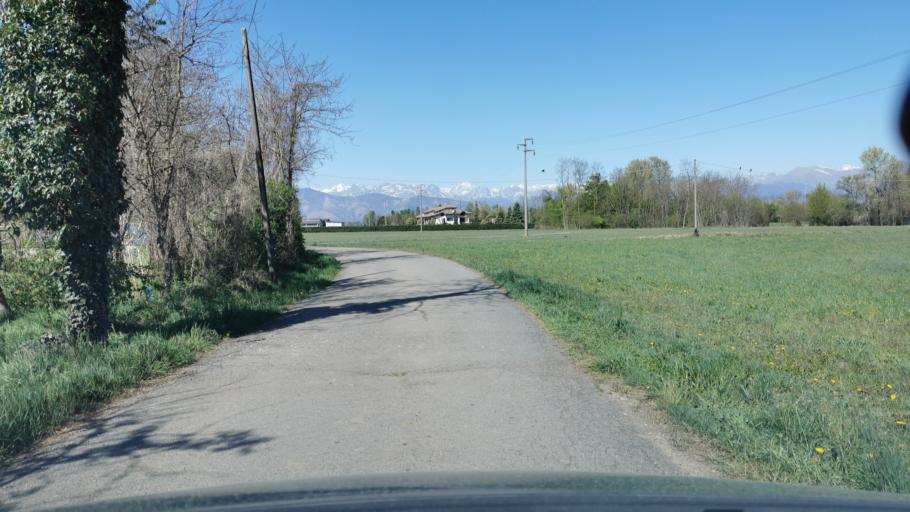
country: IT
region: Piedmont
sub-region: Provincia di Torino
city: Leini
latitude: 45.2033
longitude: 7.6970
